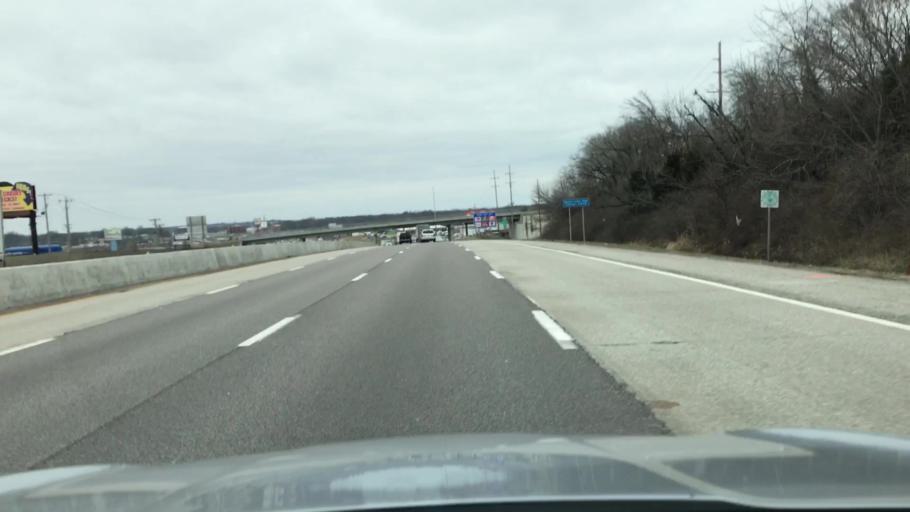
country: US
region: Missouri
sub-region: Saint Charles County
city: Saint Charles
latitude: 38.7802
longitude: -90.5165
